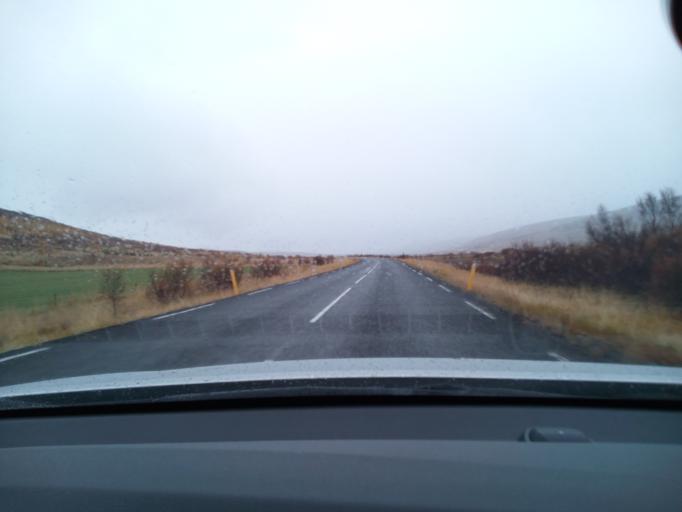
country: IS
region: South
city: Hveragerdi
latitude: 64.7015
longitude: -21.0080
